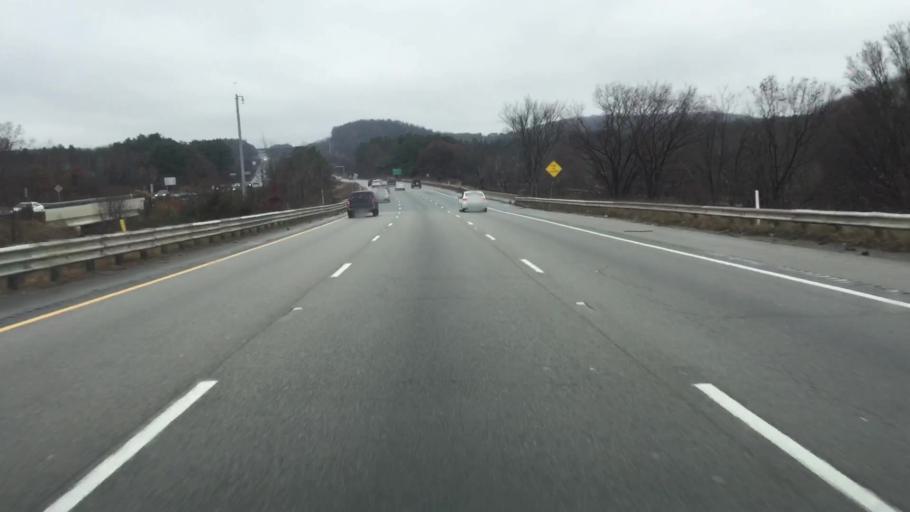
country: US
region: Massachusetts
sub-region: Worcester County
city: Southborough
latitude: 42.3063
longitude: -71.5652
